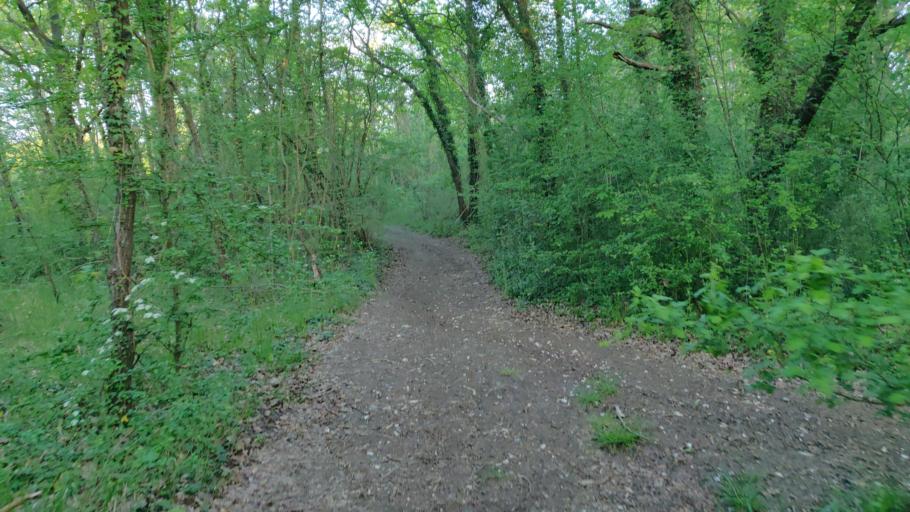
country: FR
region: Ile-de-France
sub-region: Departement des Yvelines
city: Freneuse
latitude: 49.0404
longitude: 1.6290
